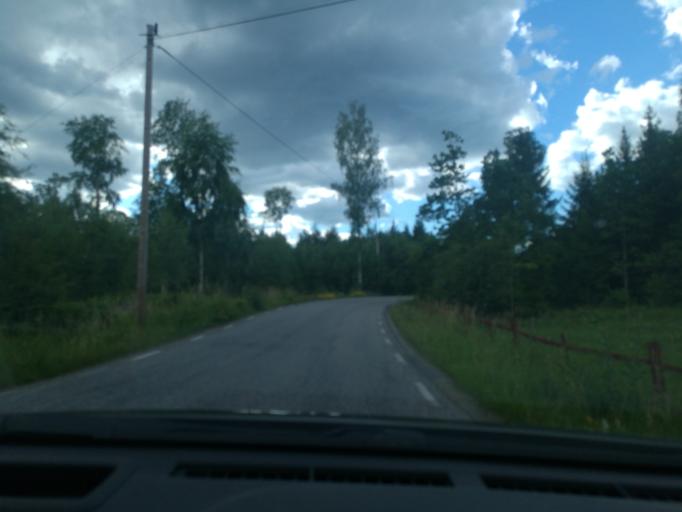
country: SE
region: Soedermanland
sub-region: Eskilstuna Kommun
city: Arla
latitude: 59.4336
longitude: 16.8140
